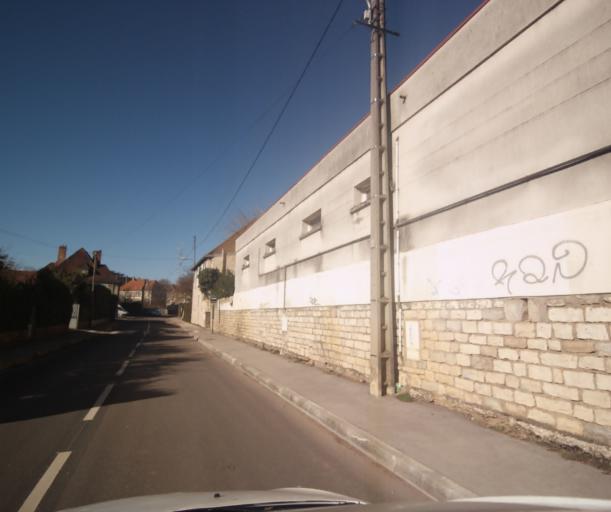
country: FR
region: Franche-Comte
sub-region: Departement du Doubs
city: Besancon
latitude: 47.2425
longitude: 6.0042
